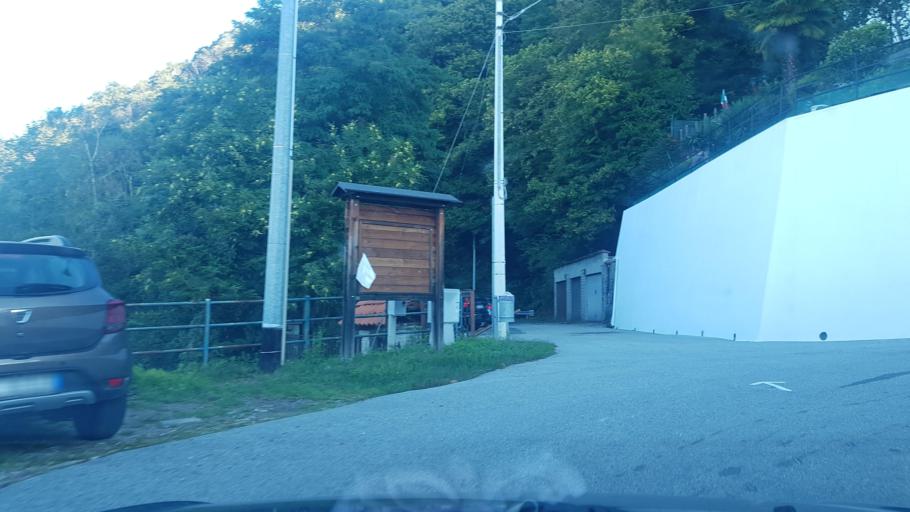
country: IT
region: Piedmont
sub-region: Provincia Verbano-Cusio-Ossola
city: Bee
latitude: 45.9670
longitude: 8.5711
